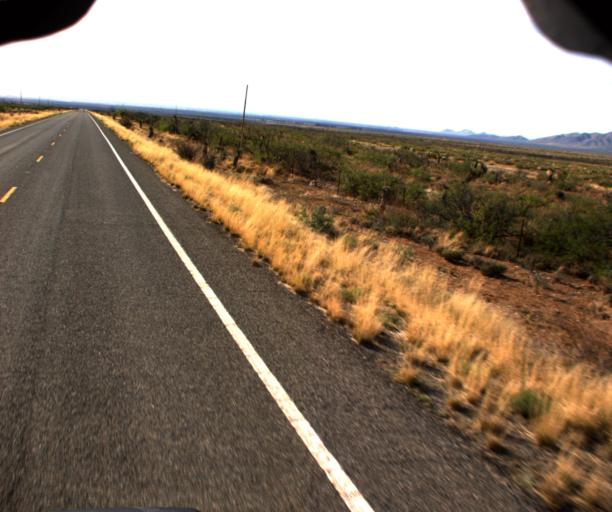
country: US
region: Arizona
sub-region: Cochise County
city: Willcox
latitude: 32.1886
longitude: -109.6853
